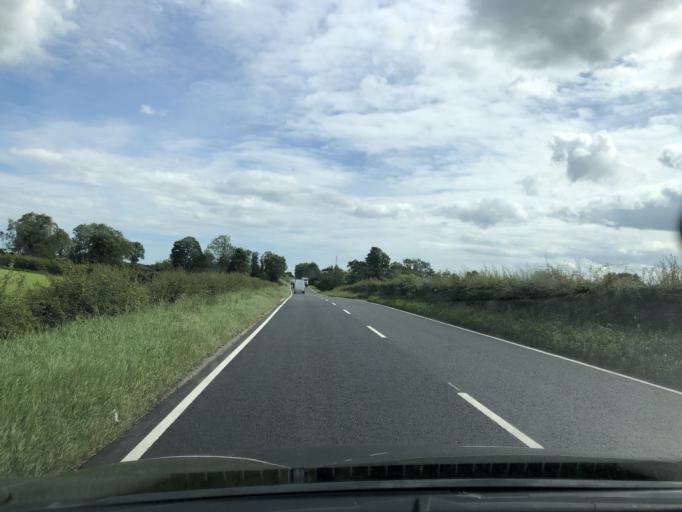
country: GB
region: Northern Ireland
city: Annahilt
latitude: 54.4499
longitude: -5.9527
